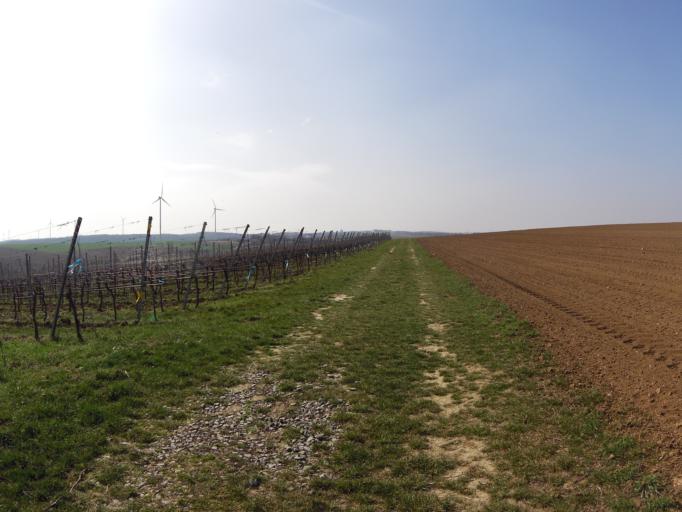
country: DE
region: Bavaria
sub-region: Regierungsbezirk Unterfranken
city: Mainstockheim
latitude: 49.7892
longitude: 10.1397
